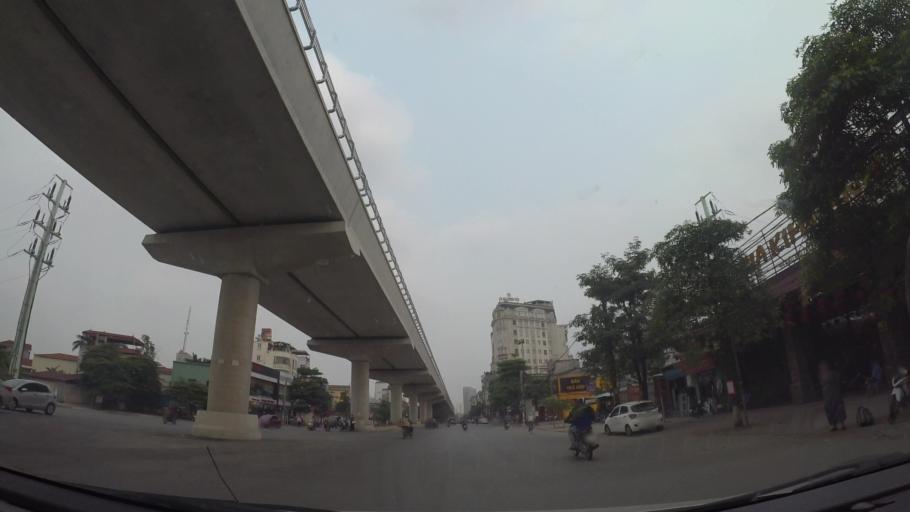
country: VN
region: Ha Noi
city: Cau Dien
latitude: 21.0465
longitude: 105.7483
